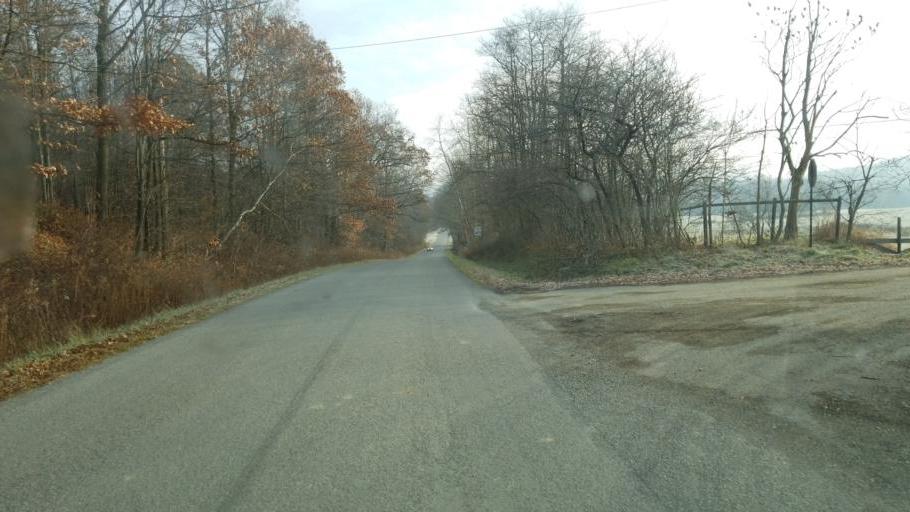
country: US
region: Pennsylvania
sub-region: Crawford County
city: Cochranton
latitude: 41.5110
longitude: -80.0759
